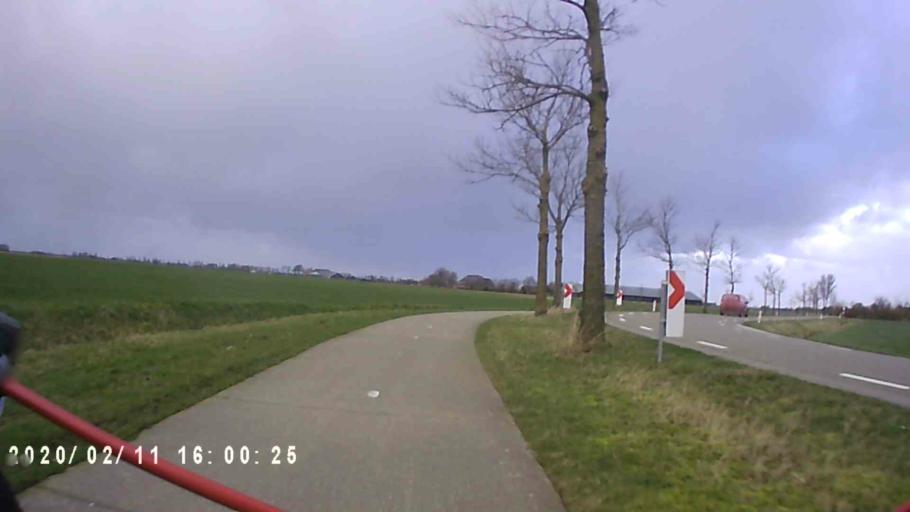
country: NL
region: Groningen
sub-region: Gemeente Zuidhorn
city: Oldehove
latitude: 53.2936
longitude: 6.4208
